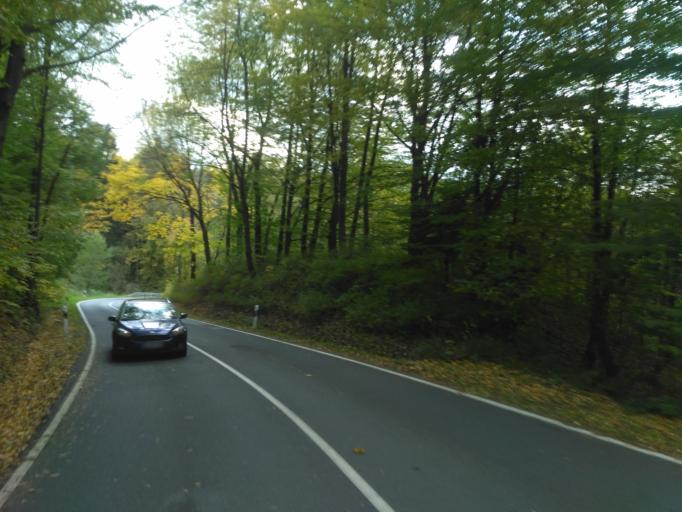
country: DE
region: Saxony
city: Hohnstein
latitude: 50.9825
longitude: 14.1070
